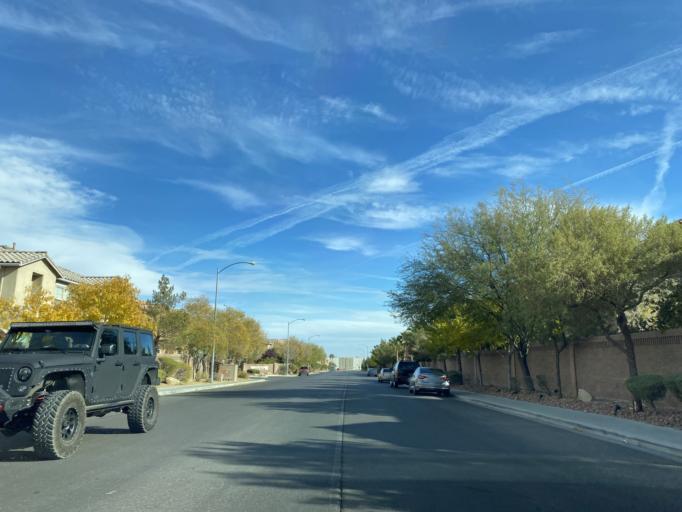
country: US
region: Nevada
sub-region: Clark County
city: Enterprise
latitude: 36.0599
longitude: -115.2292
